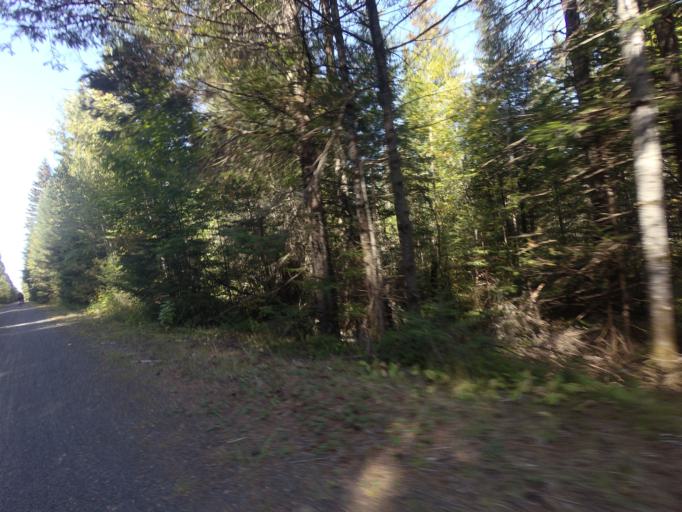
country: CA
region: Quebec
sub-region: Laurentides
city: Sainte-Agathe-des-Monts
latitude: 46.0956
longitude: -74.3547
